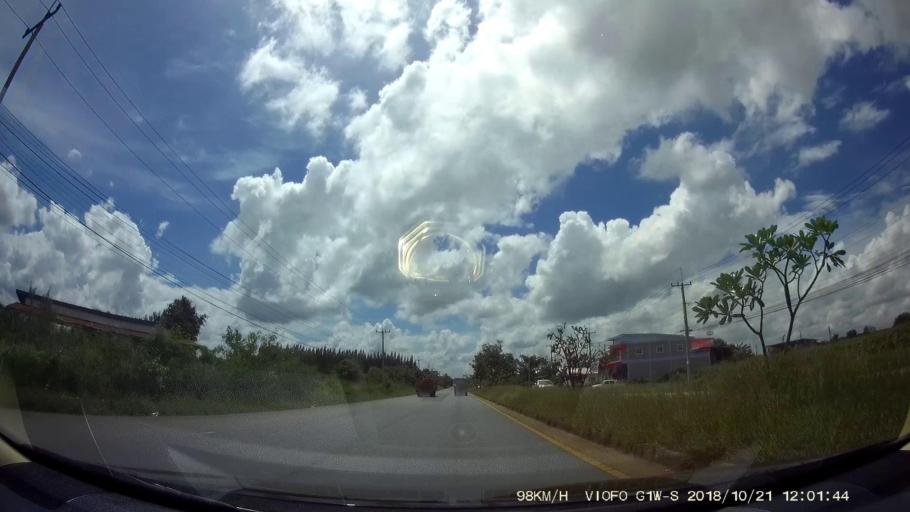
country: TH
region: Chaiyaphum
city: Chatturat
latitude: 15.5342
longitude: 101.8332
